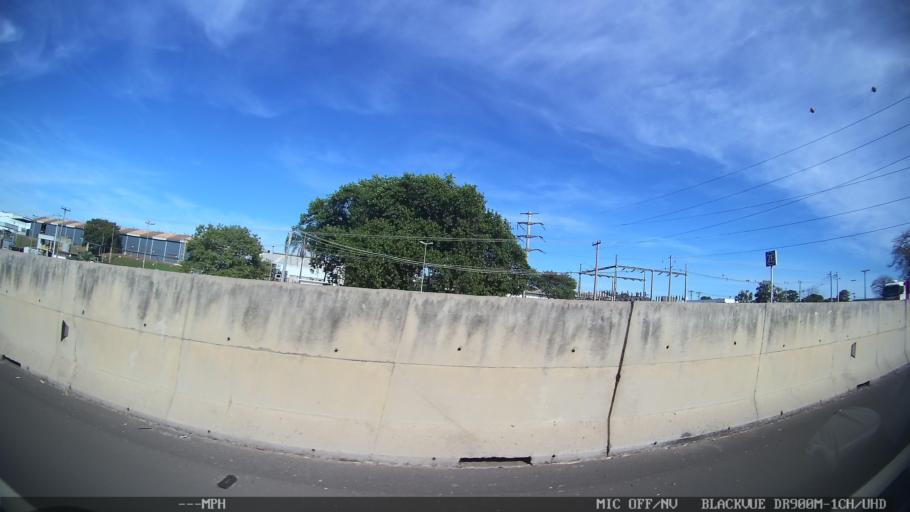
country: BR
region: Sao Paulo
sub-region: Limeira
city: Limeira
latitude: -22.5488
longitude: -47.3710
